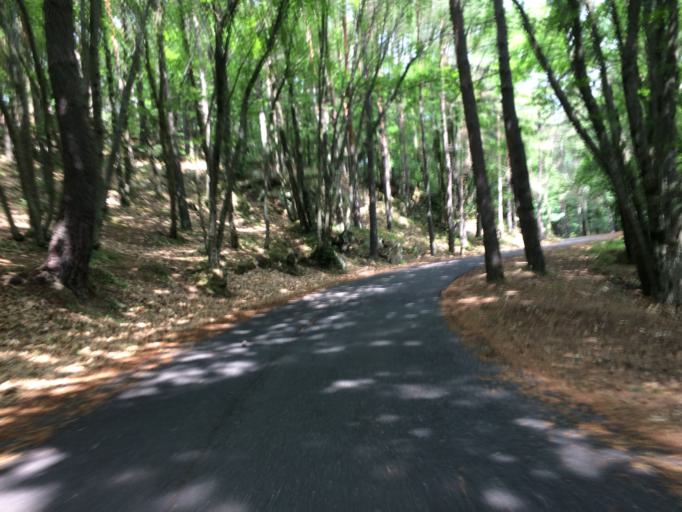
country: IT
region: Liguria
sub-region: Provincia di Imperia
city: Bajardo
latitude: 43.8973
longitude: 7.7296
